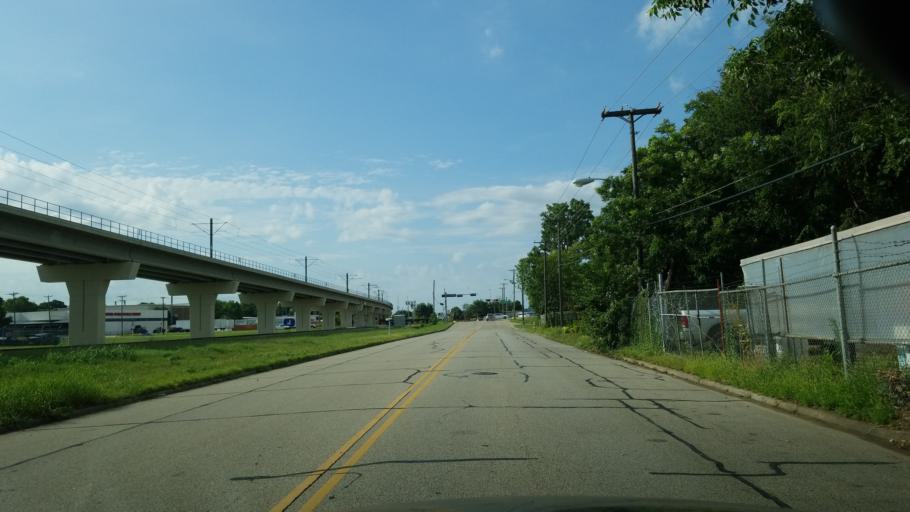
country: US
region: Texas
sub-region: Dallas County
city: Carrollton
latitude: 32.9661
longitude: -96.9163
